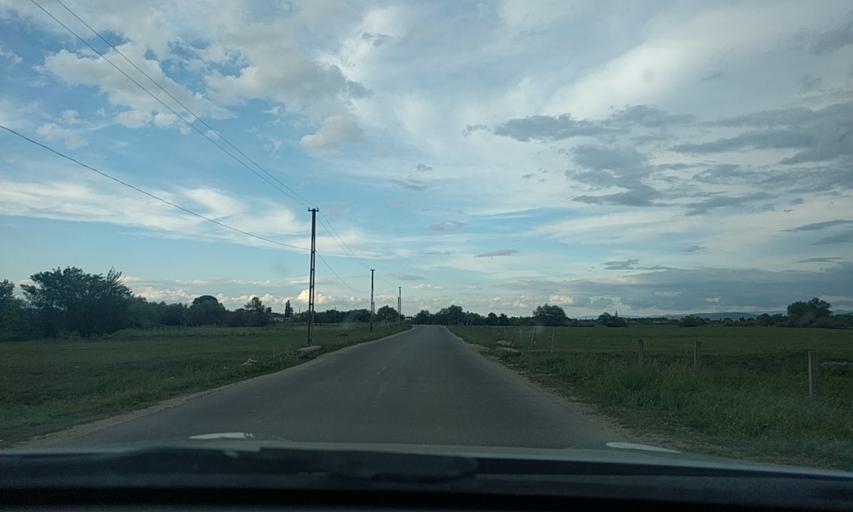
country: RO
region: Brasov
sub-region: Comuna Harman
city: Harman
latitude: 45.7512
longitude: 25.7104
